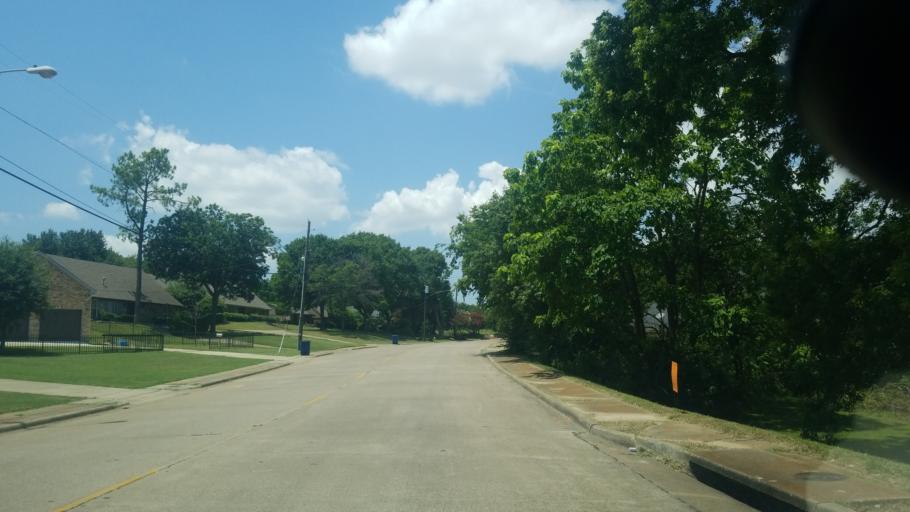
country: US
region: Texas
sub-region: Dallas County
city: Dallas
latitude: 32.7272
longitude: -96.7905
